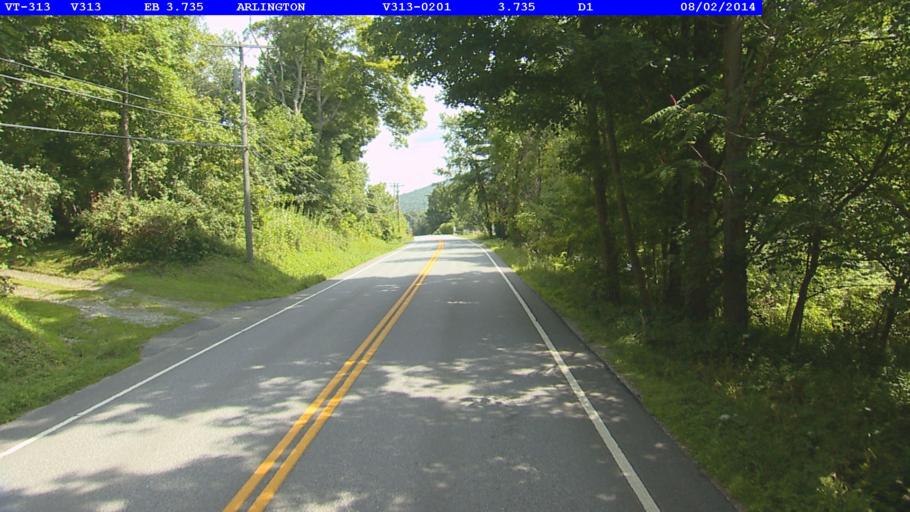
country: US
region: Vermont
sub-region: Bennington County
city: Arlington
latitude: 43.0941
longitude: -73.2005
